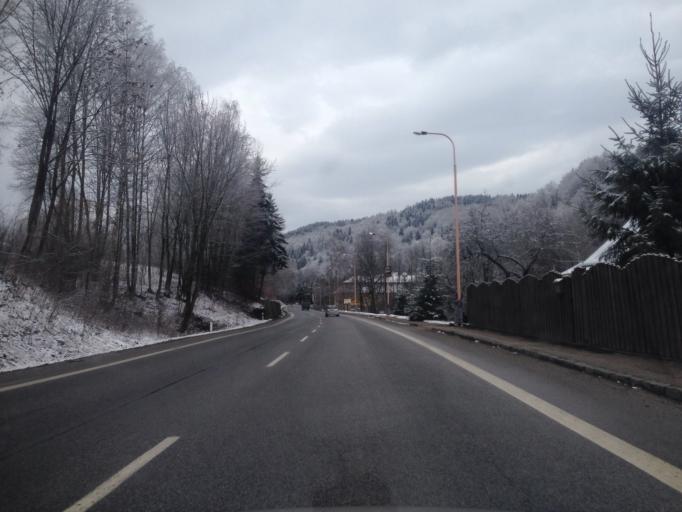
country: CZ
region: Liberecky
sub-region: Okres Semily
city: Ponikla
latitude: 50.6307
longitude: 15.4701
